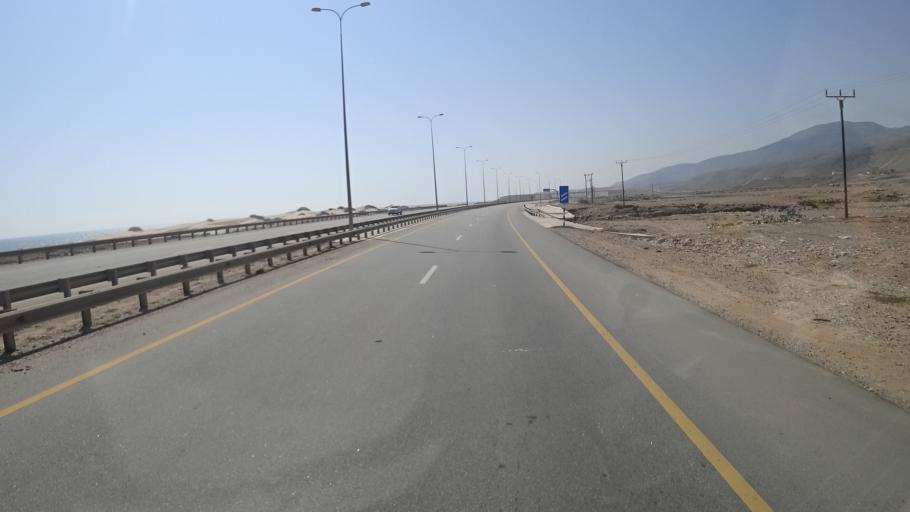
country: OM
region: Zufar
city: Salalah
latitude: 17.0262
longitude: 54.6482
